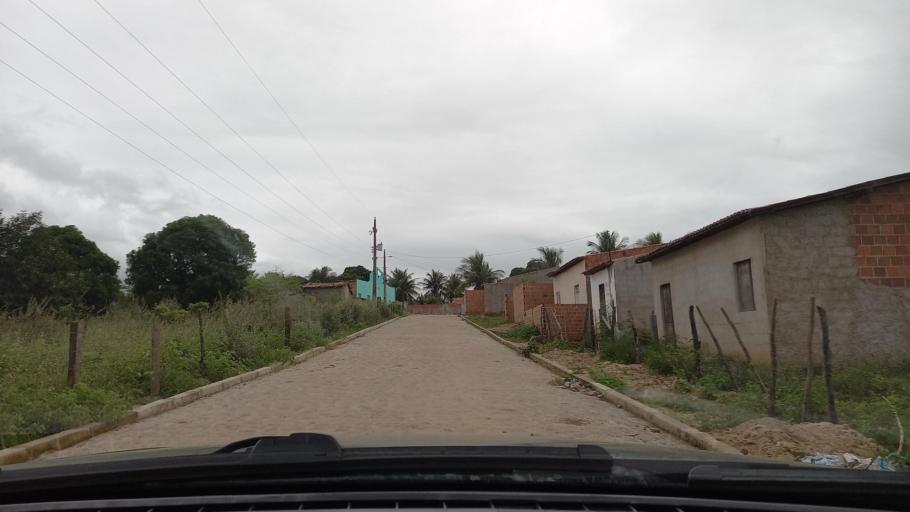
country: BR
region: Sergipe
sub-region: Caninde De Sao Francisco
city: Caninde de Sao Francisco
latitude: -9.6108
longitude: -37.7552
